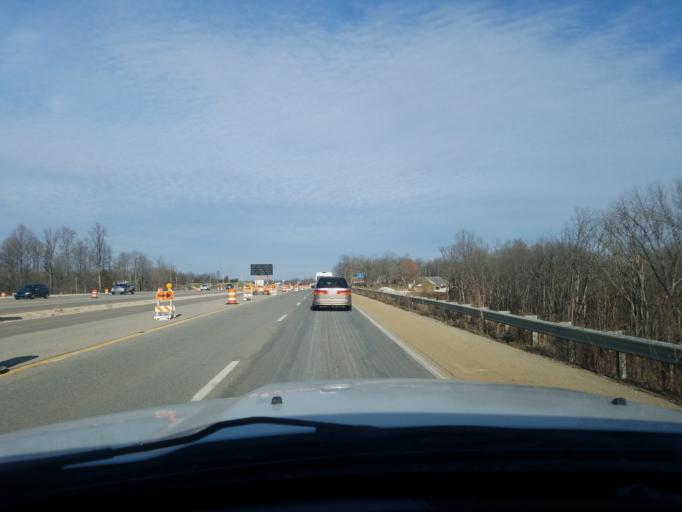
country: US
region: Indiana
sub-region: Monroe County
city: Bloomington
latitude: 39.2545
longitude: -86.5271
